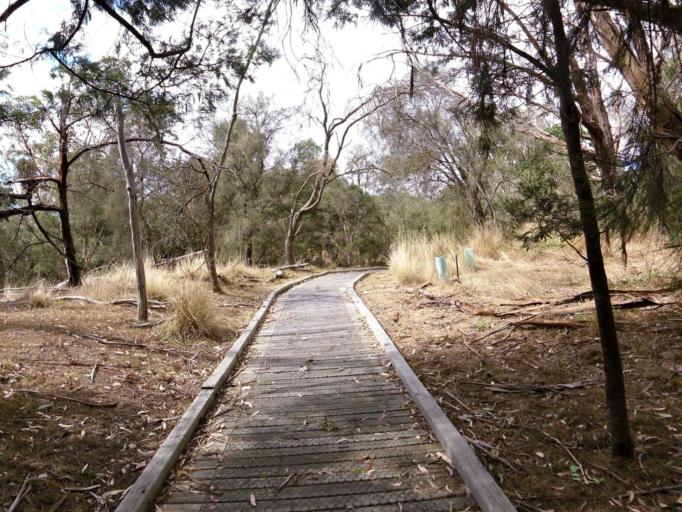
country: AU
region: Victoria
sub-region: Mornington Peninsula
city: Mount Martha
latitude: -38.2687
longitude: 145.0451
